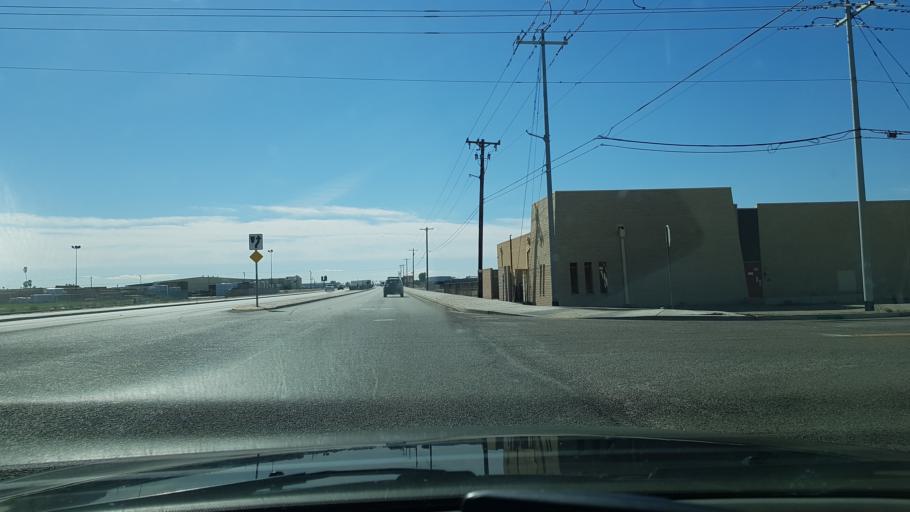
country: US
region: Arizona
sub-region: Yuma County
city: Yuma
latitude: 32.6774
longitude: -114.5817
